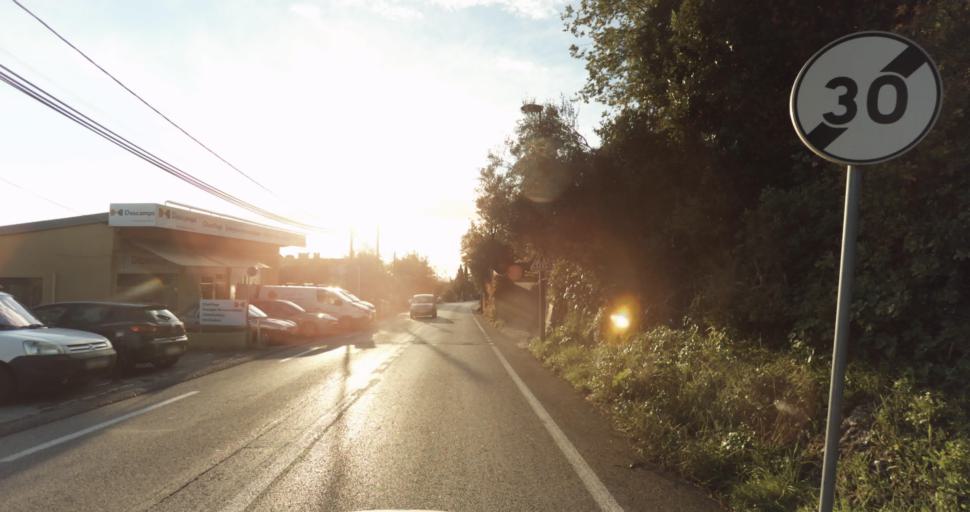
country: FR
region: Provence-Alpes-Cote d'Azur
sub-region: Departement des Alpes-Maritimes
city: Vence
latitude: 43.7196
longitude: 7.1226
